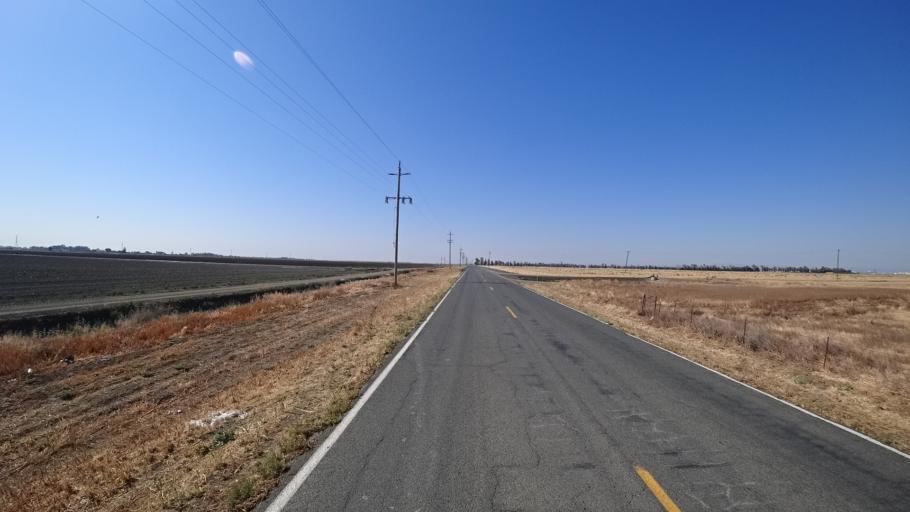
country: US
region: California
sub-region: Kings County
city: Lemoore Station
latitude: 36.3510
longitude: -119.9053
